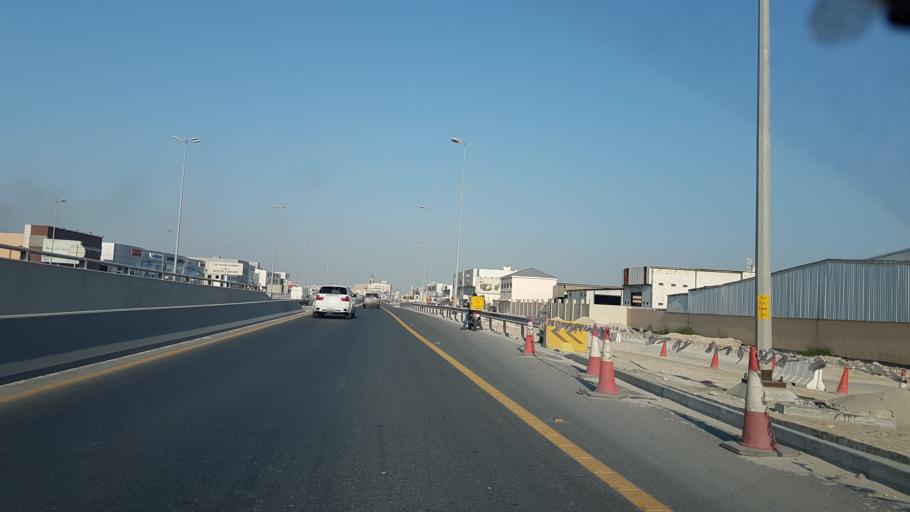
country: BH
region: Northern
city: Sitrah
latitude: 26.1322
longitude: 50.6034
